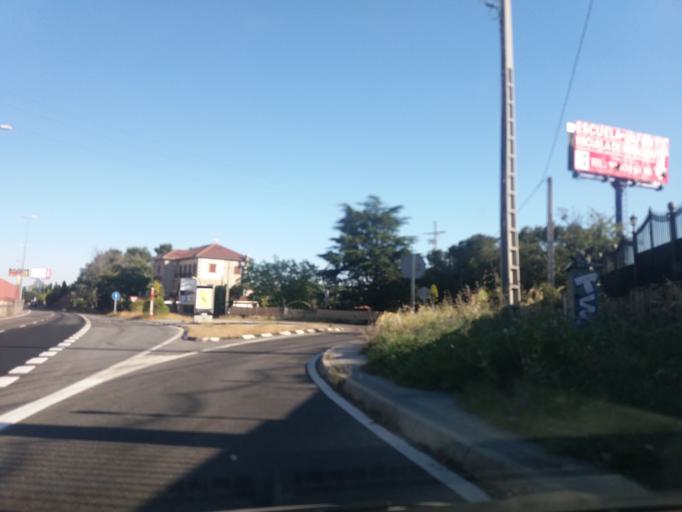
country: ES
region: Madrid
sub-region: Provincia de Madrid
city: Torrelodones
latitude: 40.5873
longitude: -3.9541
